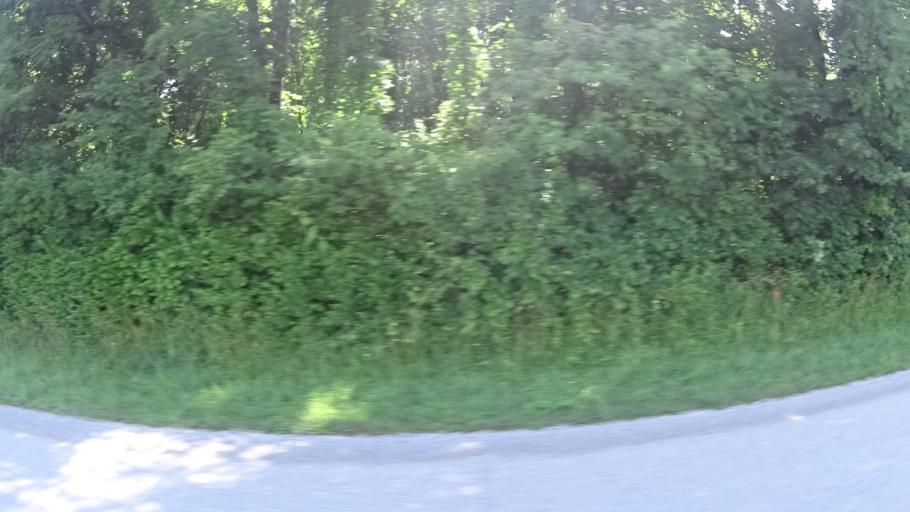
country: US
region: Ohio
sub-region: Huron County
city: Wakeman
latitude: 41.2784
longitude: -82.4125
